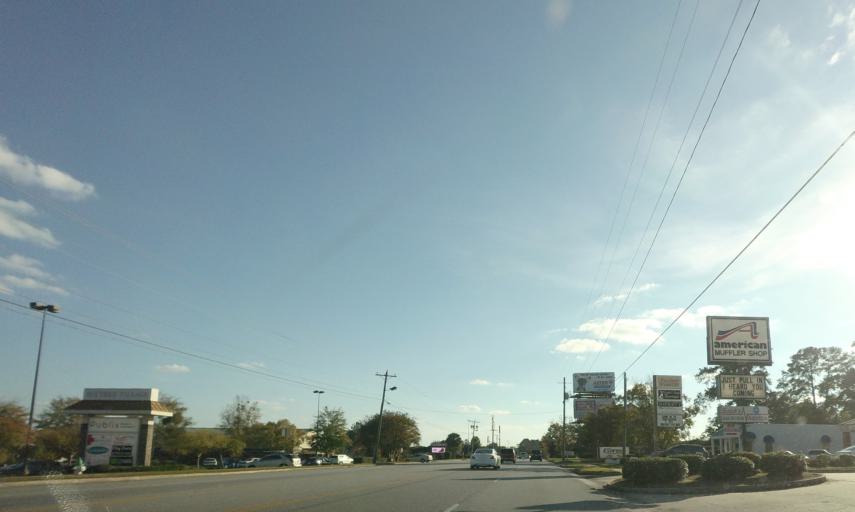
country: US
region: Georgia
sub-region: Lowndes County
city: Remerton
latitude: 30.8460
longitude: -83.3244
